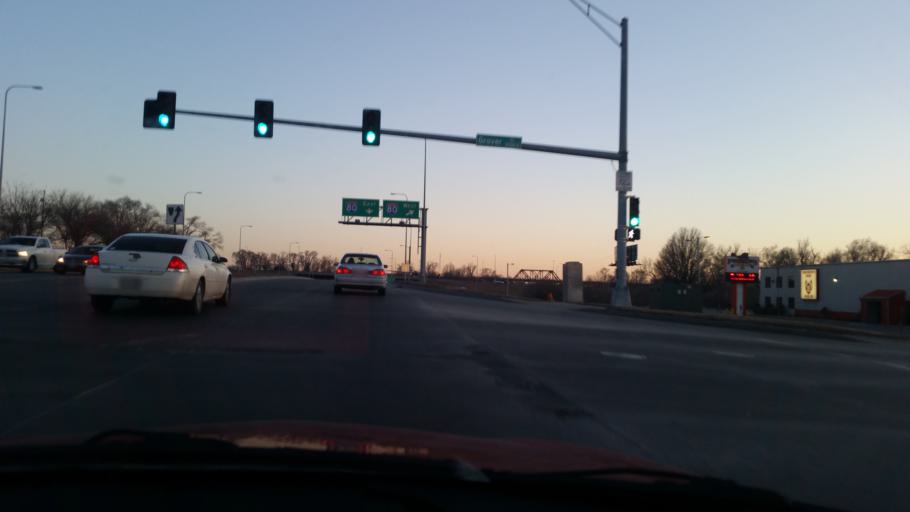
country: US
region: Nebraska
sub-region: Douglas County
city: Ralston
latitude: 41.2271
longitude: -96.0048
